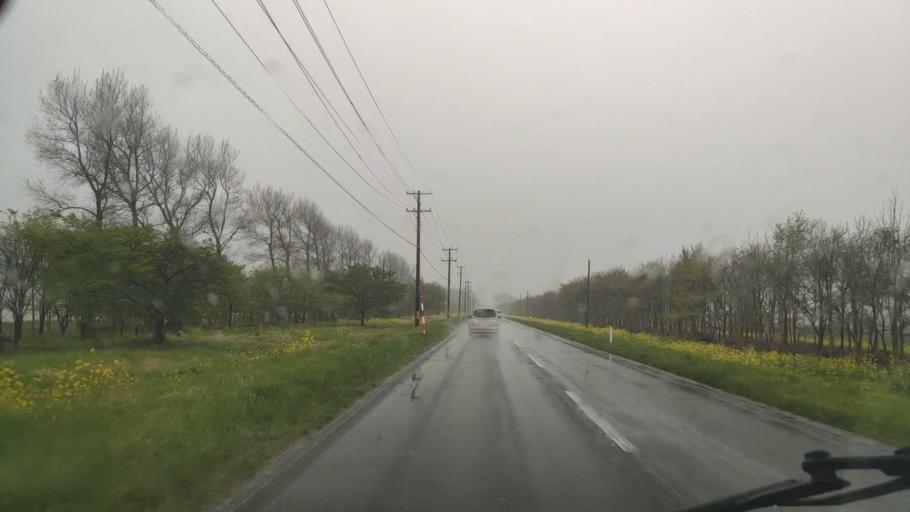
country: JP
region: Akita
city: Tenno
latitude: 39.9611
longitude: 139.9460
